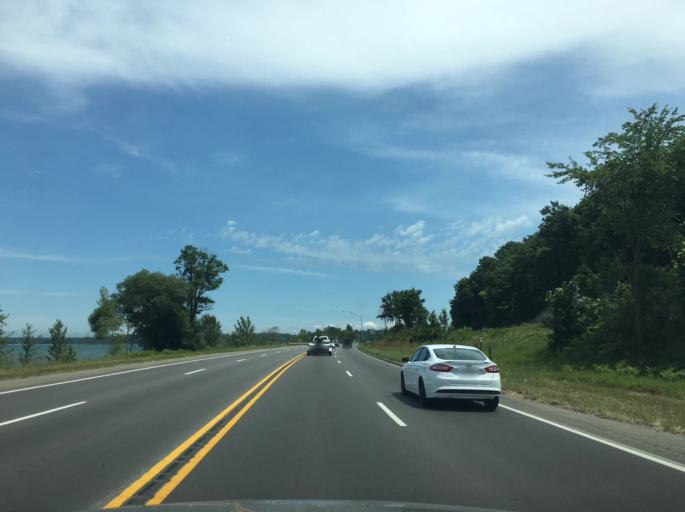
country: US
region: Michigan
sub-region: Grand Traverse County
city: Traverse City
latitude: 44.7592
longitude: -85.5157
